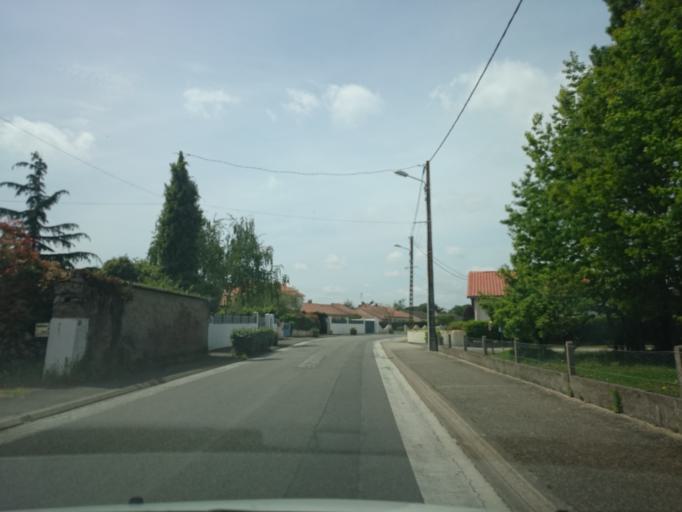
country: FR
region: Pays de la Loire
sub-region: Departement de la Loire-Atlantique
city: La Chevroliere
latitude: 47.1231
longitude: -1.6368
